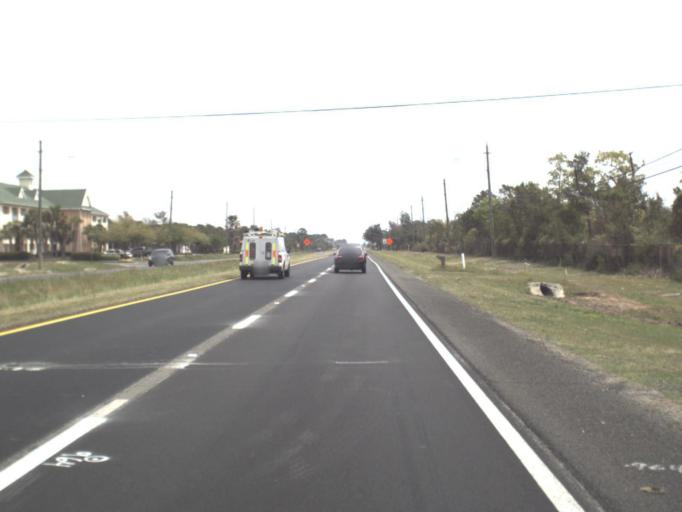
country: US
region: Florida
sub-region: Santa Rosa County
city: Navarre
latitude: 30.4018
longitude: -86.9002
